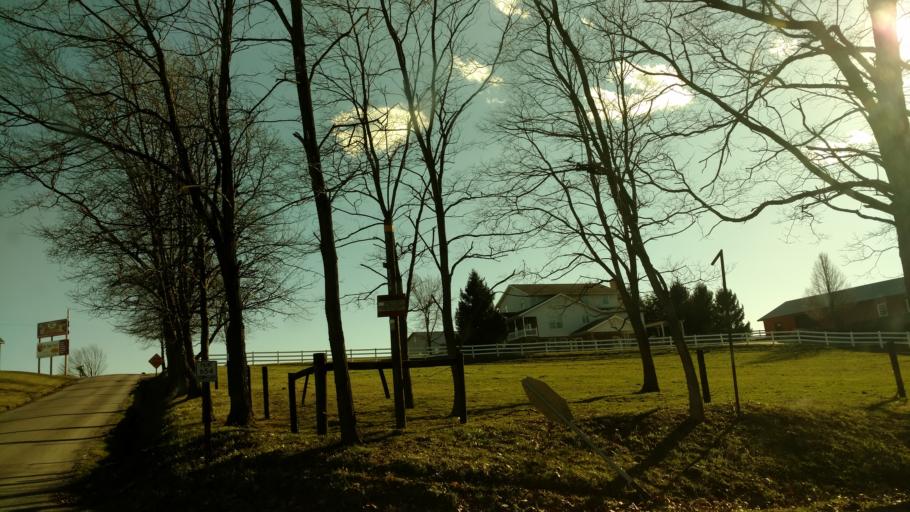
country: US
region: Ohio
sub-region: Tuscarawas County
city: Sugarcreek
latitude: 40.5982
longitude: -81.7492
